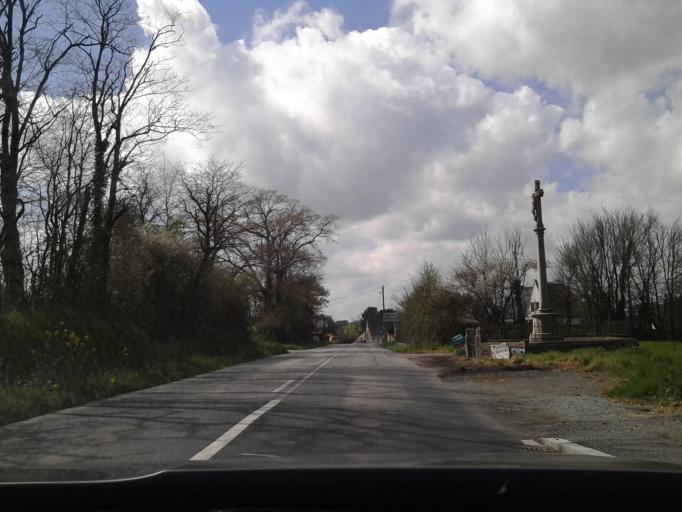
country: FR
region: Brittany
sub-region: Departement d'Ille-et-Vilaine
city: Grand-Fougeray
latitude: 47.7285
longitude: -1.7269
